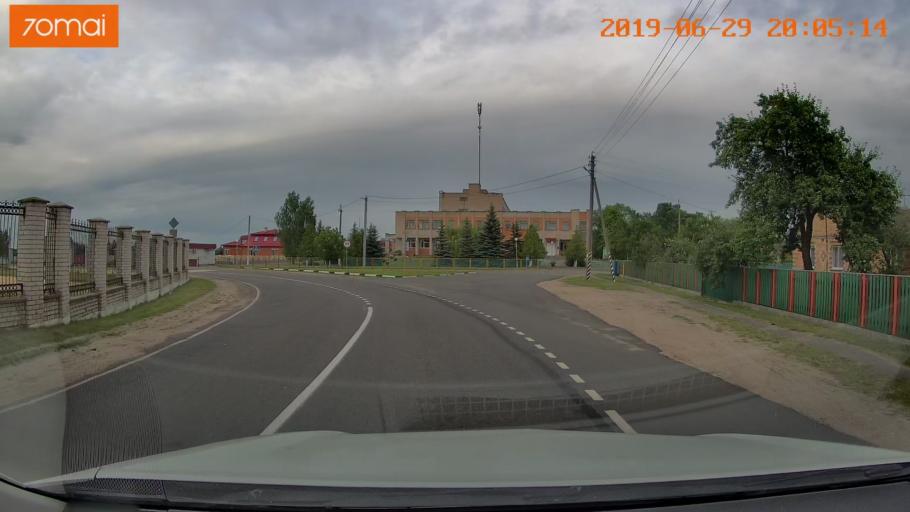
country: BY
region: Brest
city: Lahishyn
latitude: 52.3369
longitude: 26.0005
